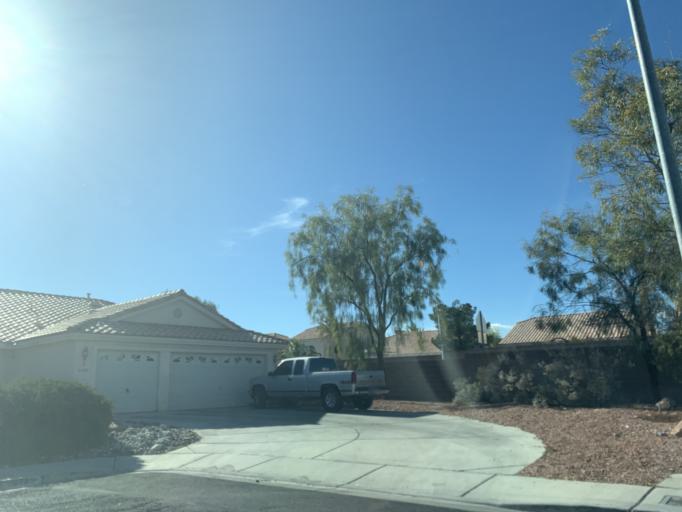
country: US
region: Nevada
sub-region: Clark County
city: Summerlin South
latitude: 36.1220
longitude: -115.3057
